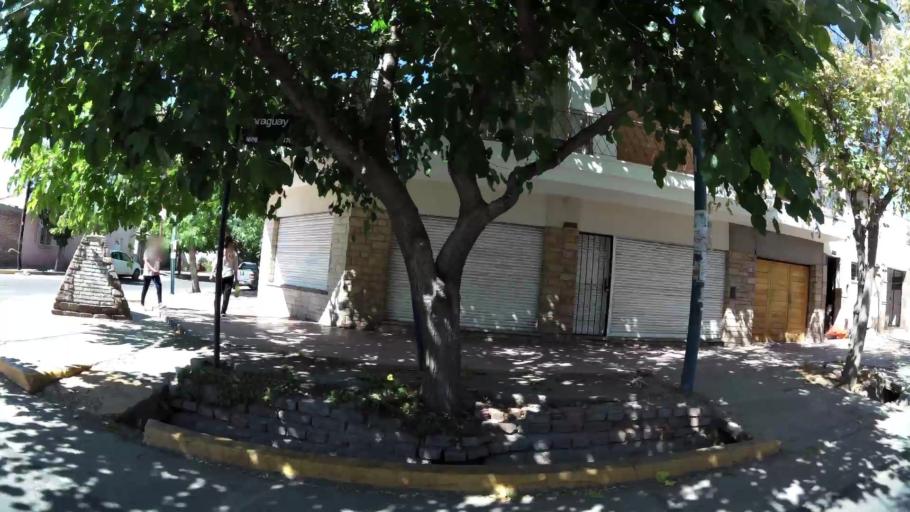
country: AR
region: Mendoza
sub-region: Departamento de Godoy Cruz
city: Godoy Cruz
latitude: -32.9047
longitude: -68.8623
